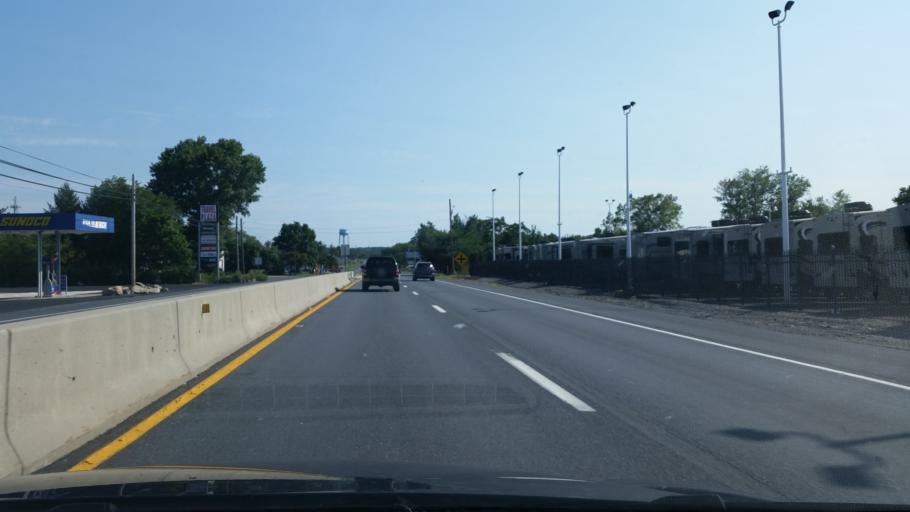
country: US
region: Pennsylvania
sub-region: Berks County
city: Shoemakersville
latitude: 40.5142
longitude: -75.9675
